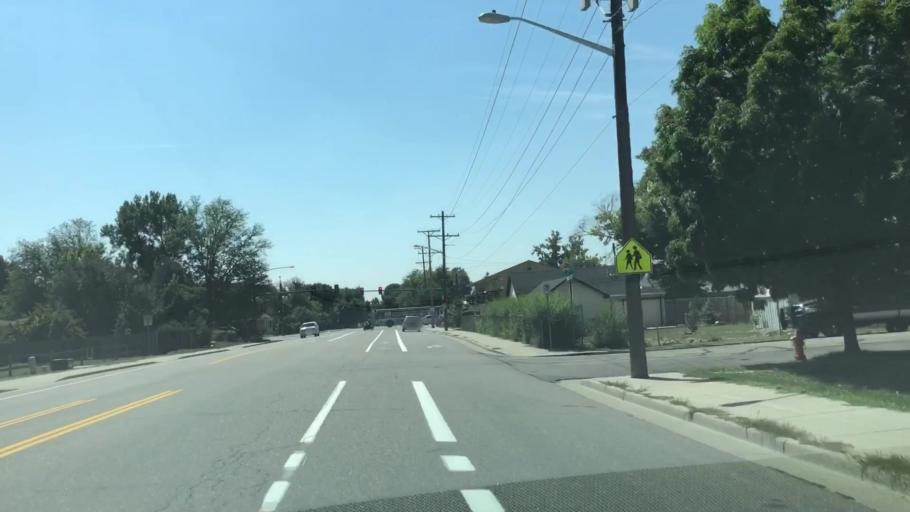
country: US
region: Colorado
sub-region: Larimer County
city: Loveland
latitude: 40.3939
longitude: -105.0590
